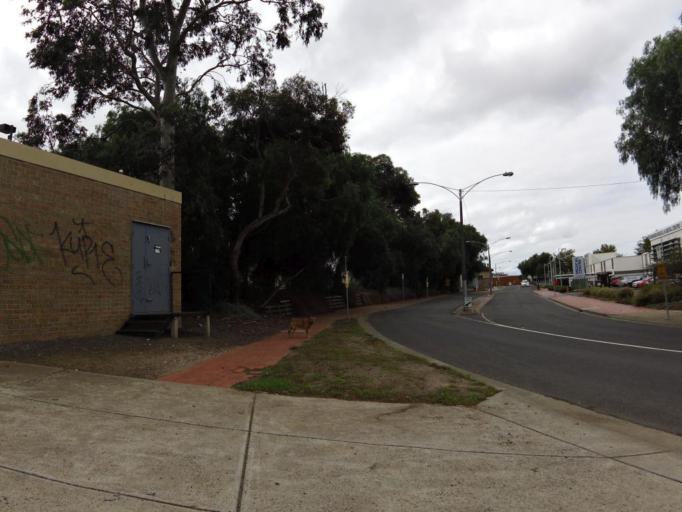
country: AU
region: Victoria
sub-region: Wyndham
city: Werribee
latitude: -37.9004
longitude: 144.6596
